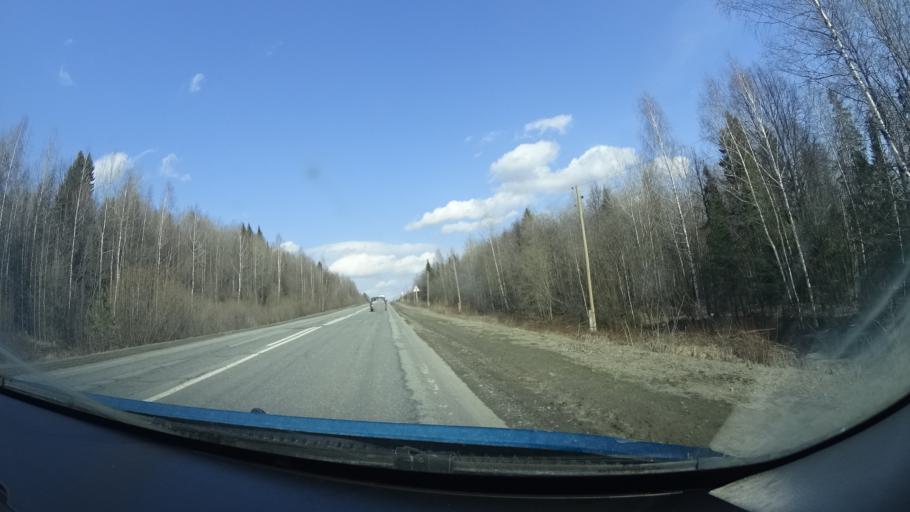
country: RU
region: Perm
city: Kultayevo
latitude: 57.8341
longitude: 55.8179
